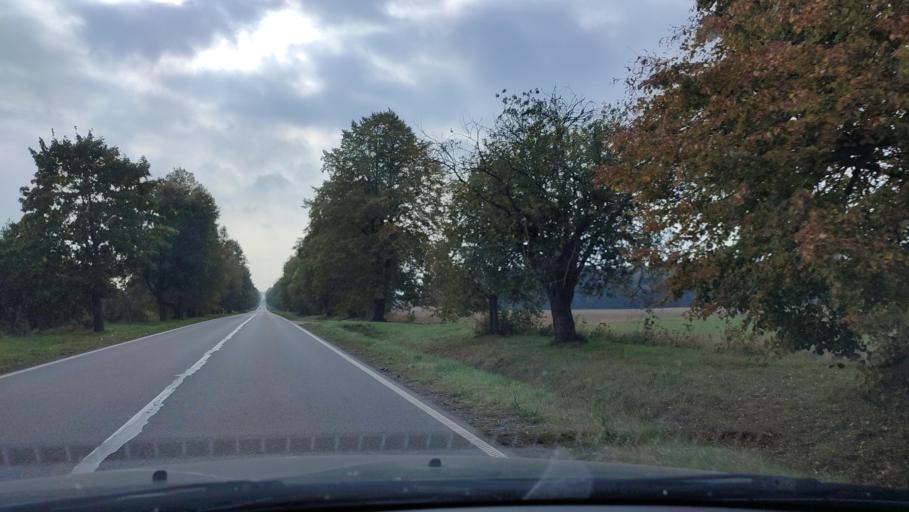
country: PL
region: Warmian-Masurian Voivodeship
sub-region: Powiat nidzicki
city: Kozlowo
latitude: 53.3469
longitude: 20.3512
